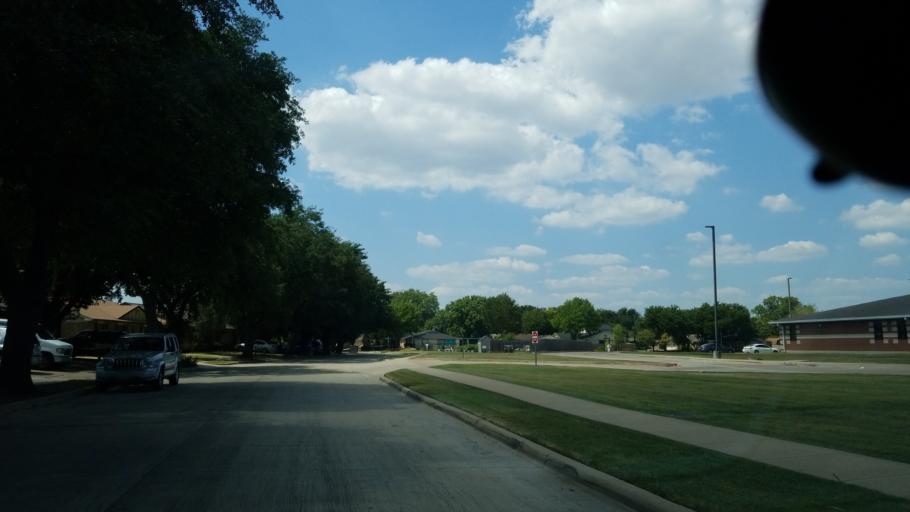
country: US
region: Texas
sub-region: Dallas County
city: Grand Prairie
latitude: 32.7018
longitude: -96.9971
